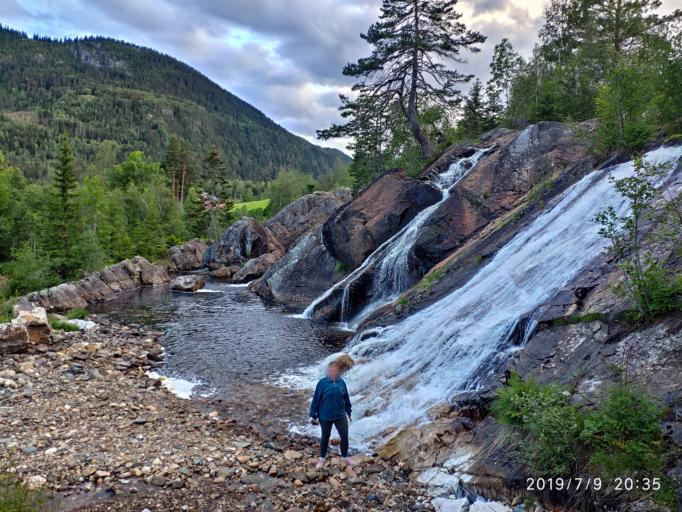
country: NO
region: Telemark
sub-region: Seljord
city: Seljord
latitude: 59.6021
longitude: 8.6443
